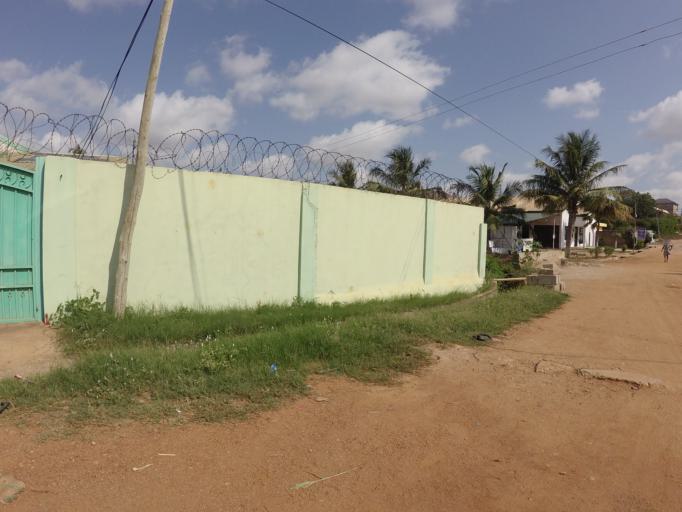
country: GH
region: Greater Accra
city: Dome
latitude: 5.6191
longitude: -0.2392
